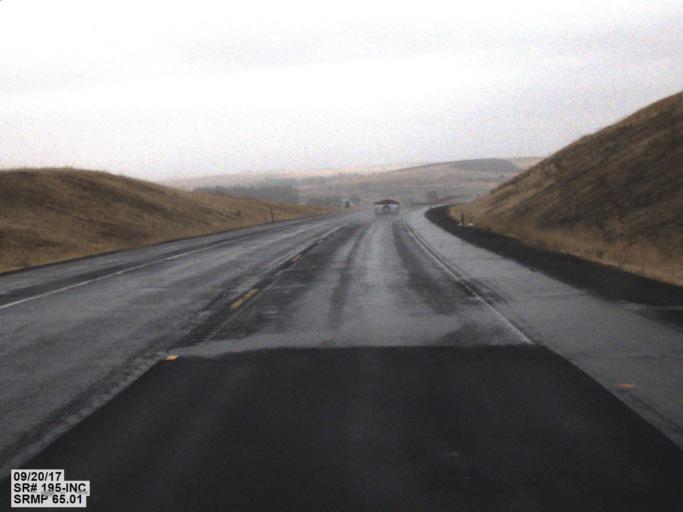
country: US
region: Washington
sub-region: Spokane County
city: Cheney
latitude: 47.2426
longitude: -117.3629
